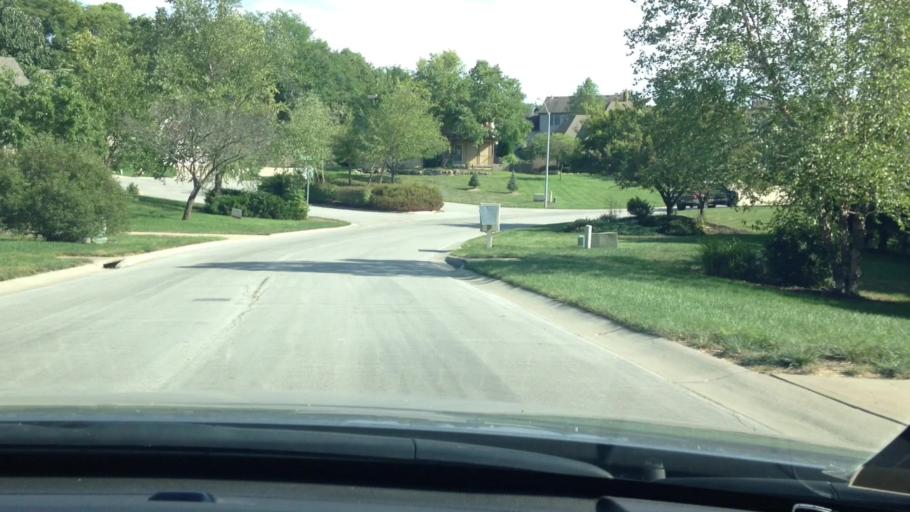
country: US
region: Missouri
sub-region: Jackson County
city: Lees Summit
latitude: 38.9244
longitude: -94.4189
